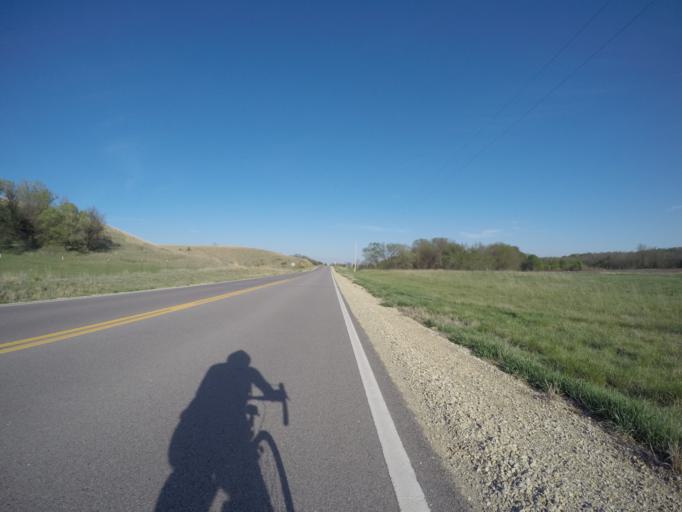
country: US
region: Kansas
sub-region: Riley County
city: Ogden
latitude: 39.2326
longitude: -96.7525
